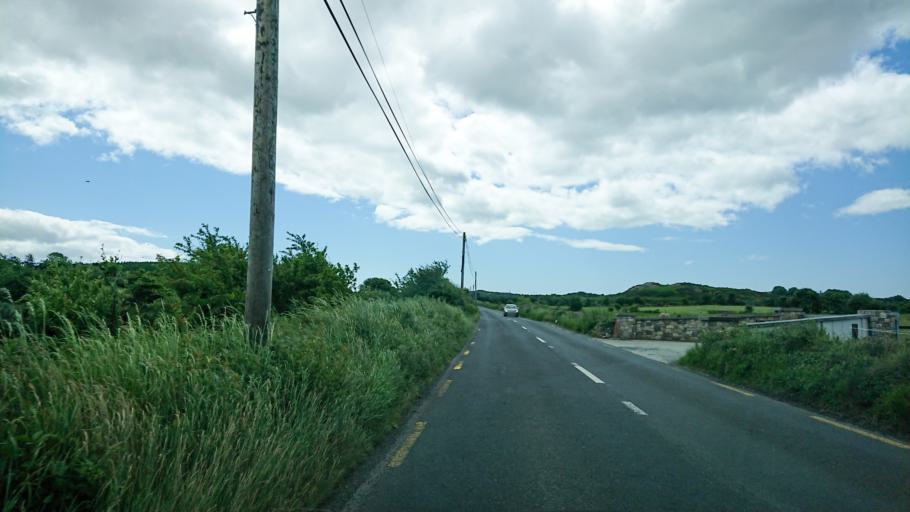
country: IE
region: Munster
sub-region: Waterford
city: Tra Mhor
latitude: 52.1885
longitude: -7.1797
